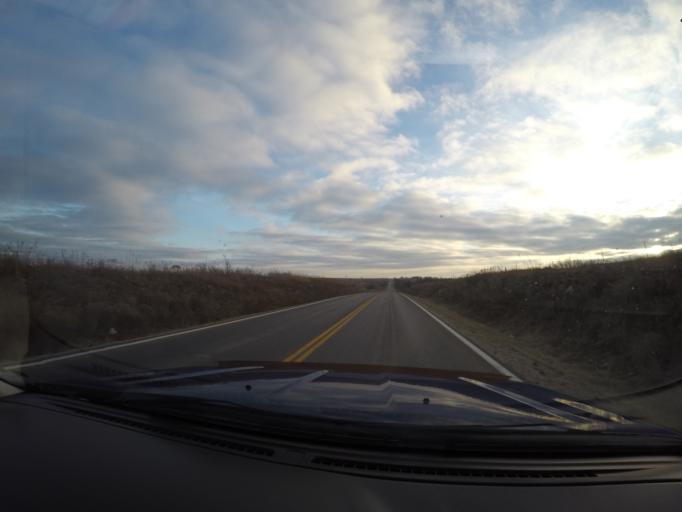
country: US
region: Kansas
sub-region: Morris County
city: Council Grove
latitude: 38.6468
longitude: -96.4896
